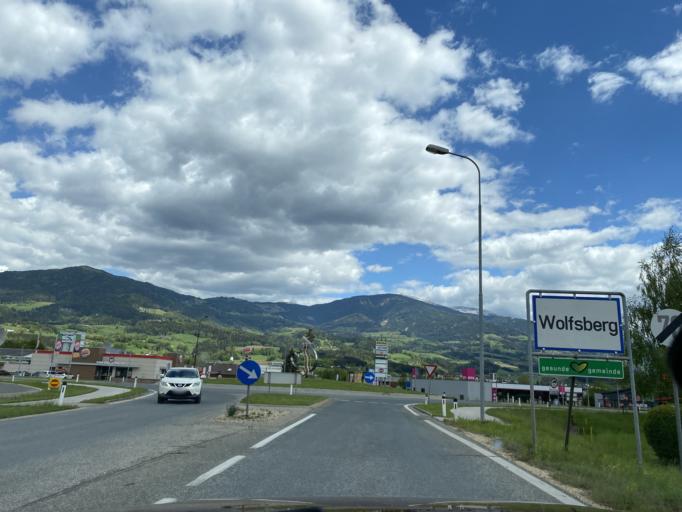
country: AT
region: Carinthia
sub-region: Politischer Bezirk Wolfsberg
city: Wolfsberg
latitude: 46.8190
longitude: 14.8352
